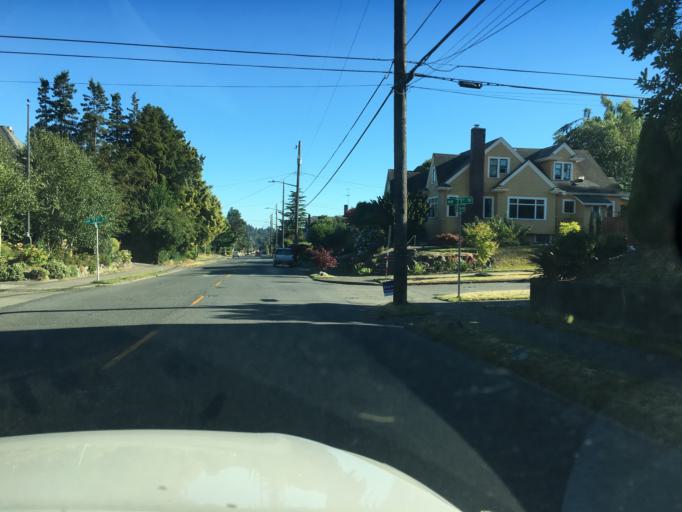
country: US
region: Washington
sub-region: King County
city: Shoreline
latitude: 47.6805
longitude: -122.3984
